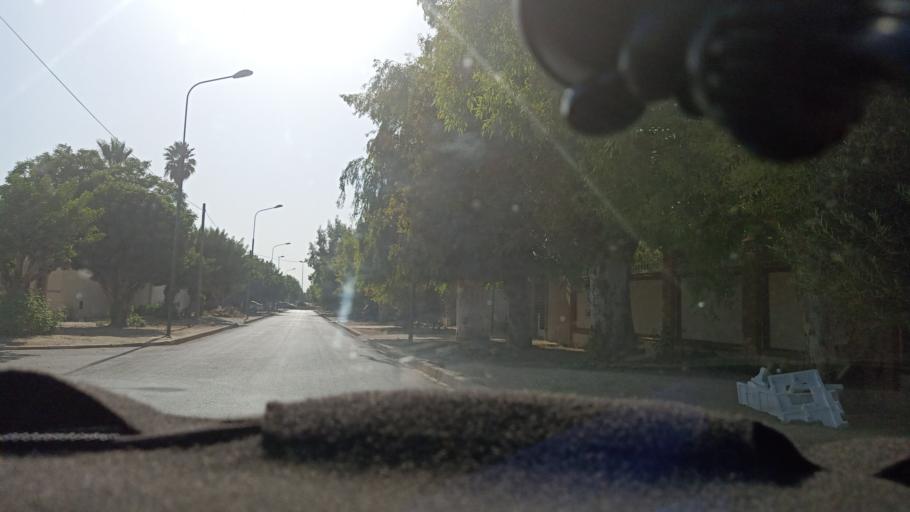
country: MA
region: Doukkala-Abda
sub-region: Safi
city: Youssoufia
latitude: 32.2468
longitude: -8.5247
